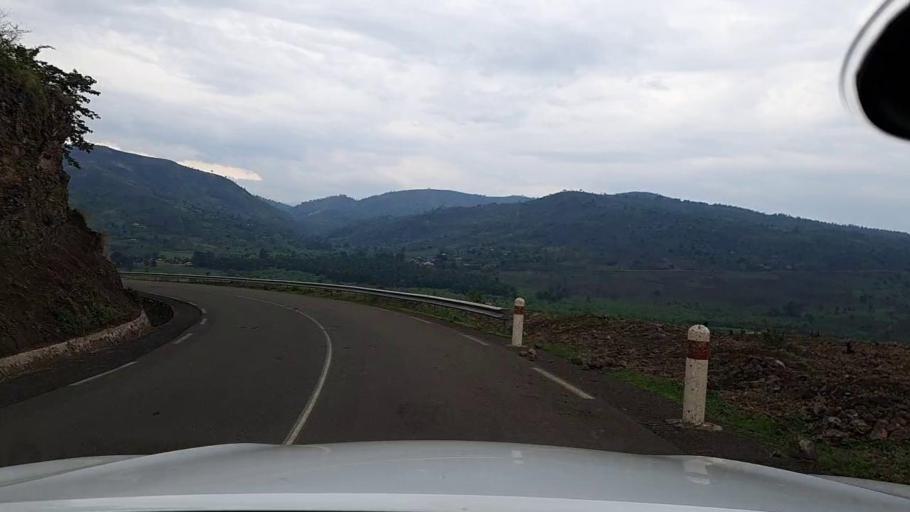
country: BI
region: Cibitoke
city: Cibitoke
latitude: -2.7354
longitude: 29.0366
